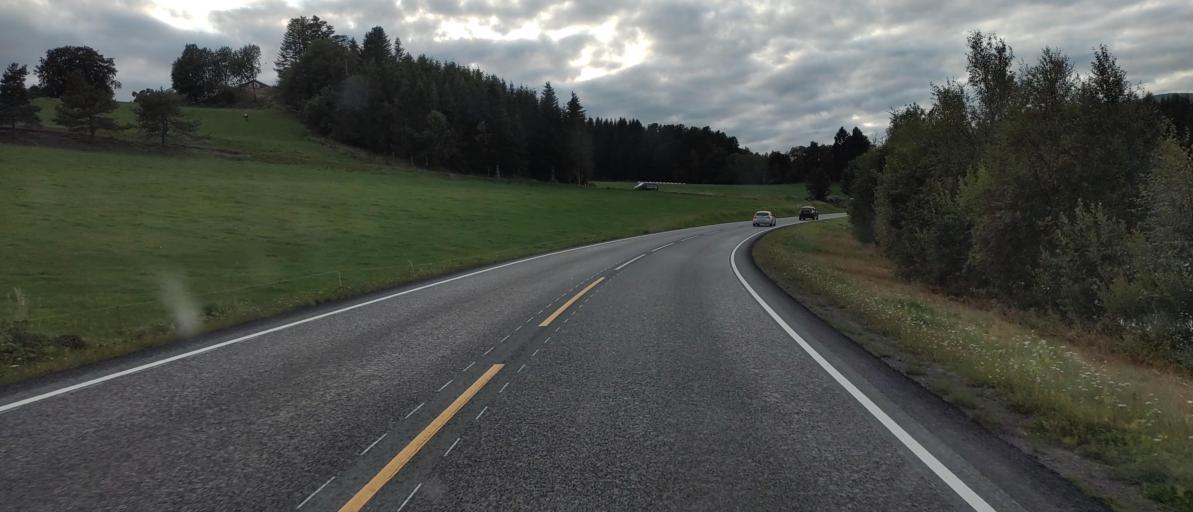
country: NO
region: More og Romsdal
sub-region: Molde
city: Hjelset
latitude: 62.7326
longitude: 7.3322
